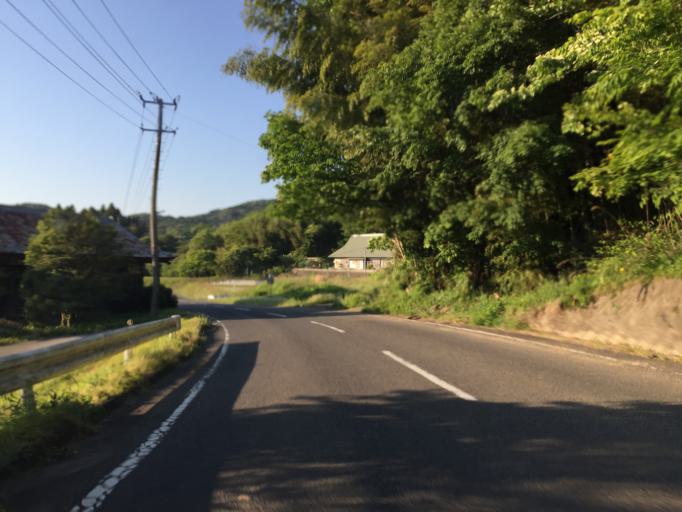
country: JP
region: Fukushima
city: Ishikawa
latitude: 37.0384
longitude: 140.4357
